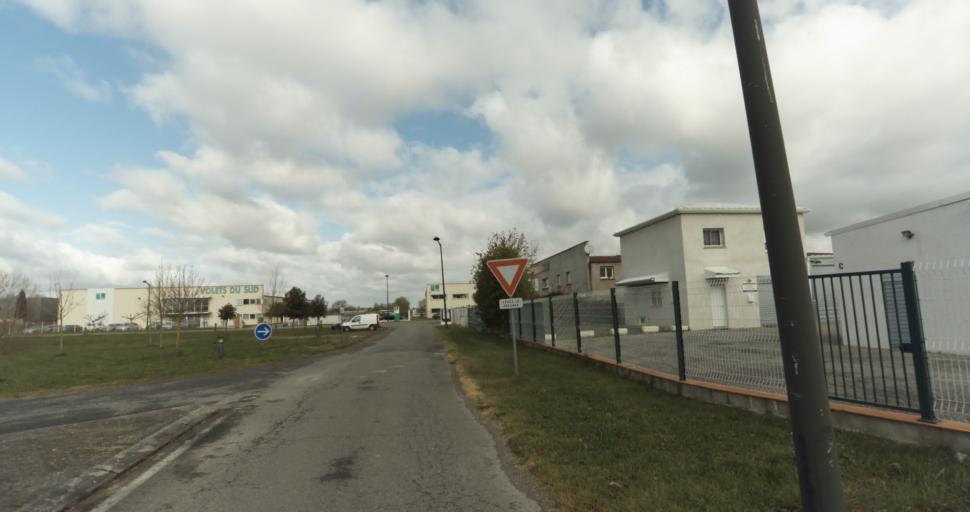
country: FR
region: Midi-Pyrenees
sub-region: Departement de la Haute-Garonne
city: Miremont
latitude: 43.3694
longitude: 1.4467
